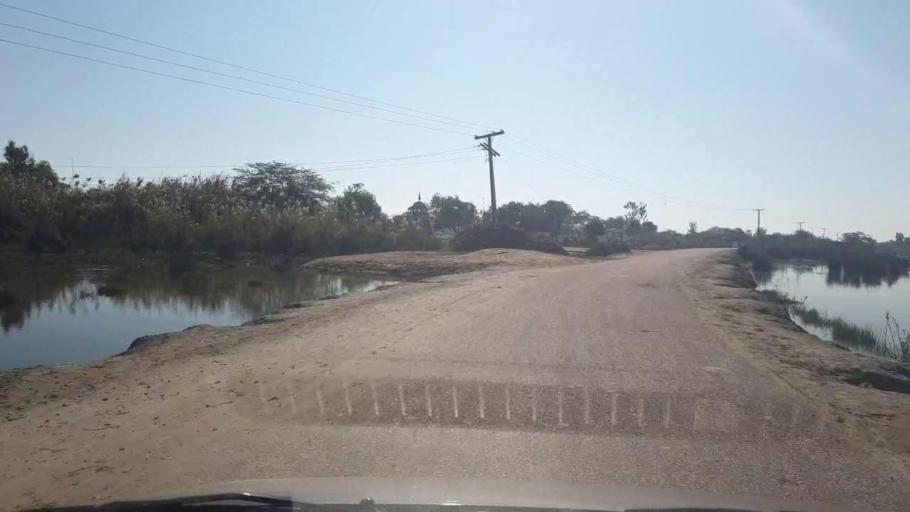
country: PK
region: Sindh
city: Bozdar
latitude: 27.1332
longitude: 68.6418
